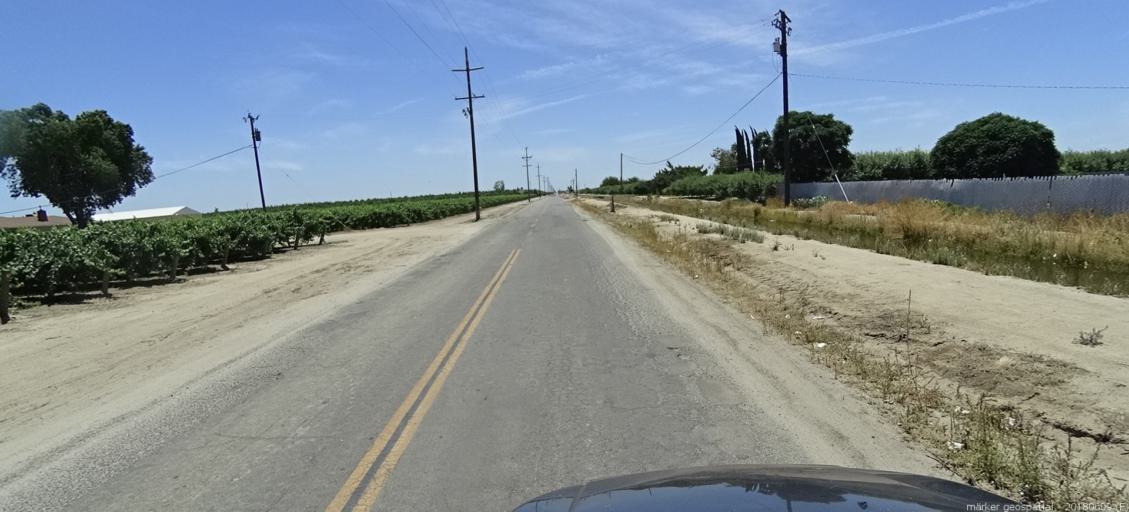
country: US
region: California
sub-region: Madera County
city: Parkwood
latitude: 36.8798
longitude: -120.1104
